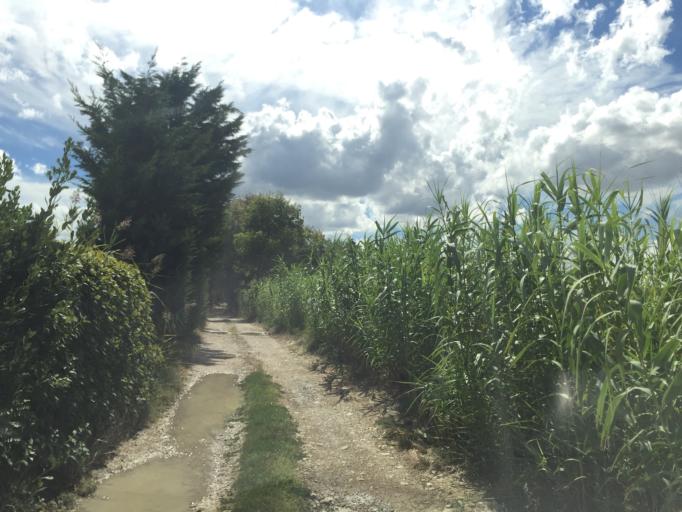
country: FR
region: Provence-Alpes-Cote d'Azur
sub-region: Departement du Vaucluse
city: Caderousse
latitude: 44.1046
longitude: 4.7666
